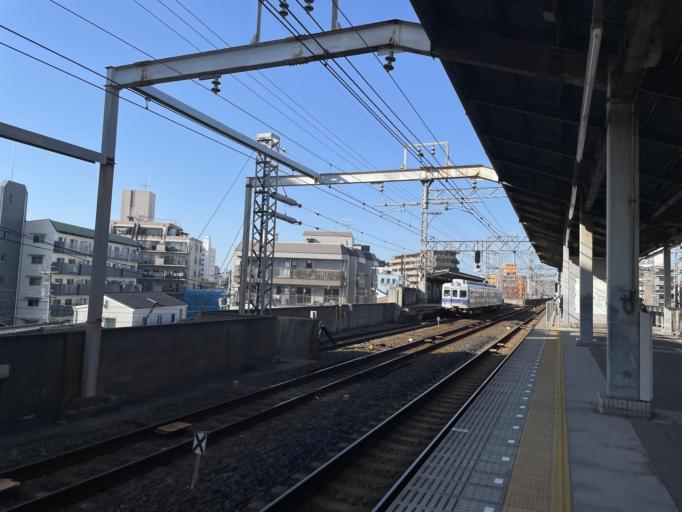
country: JP
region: Osaka
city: Sakai
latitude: 34.6288
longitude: 135.4945
